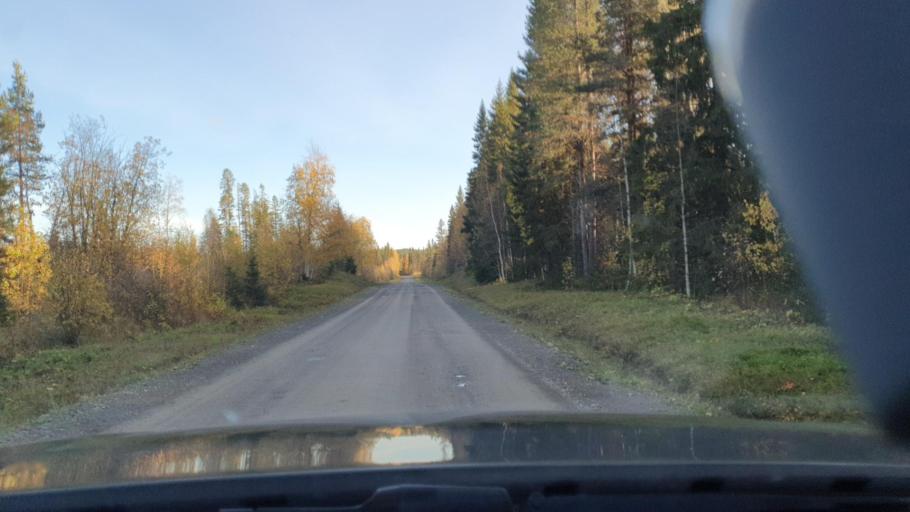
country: SE
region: Jaemtland
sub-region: Stroemsunds Kommun
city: Stroemsund
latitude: 63.5226
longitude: 15.6341
